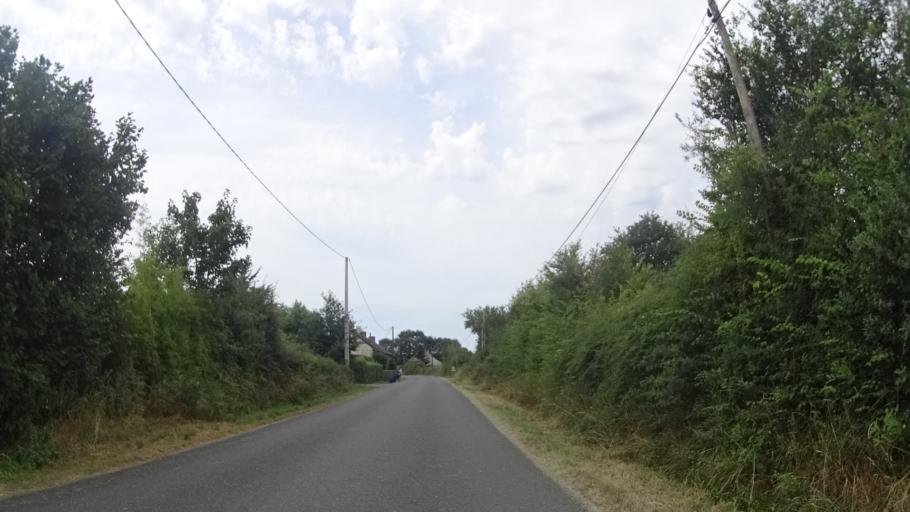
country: FR
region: Pays de la Loire
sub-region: Departement de la Loire-Atlantique
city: Fay-de-Bretagne
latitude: 47.4186
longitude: -1.7728
